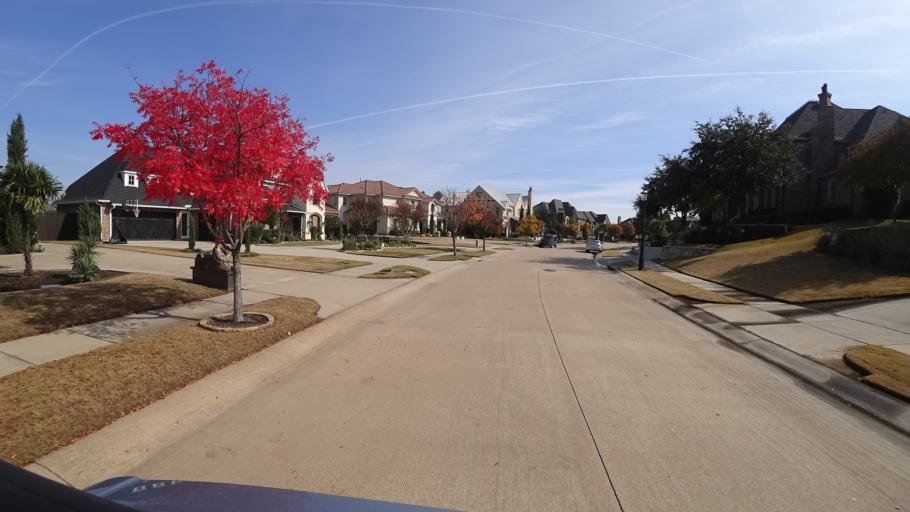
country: US
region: Texas
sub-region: Denton County
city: The Colony
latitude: 33.0416
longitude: -96.8938
